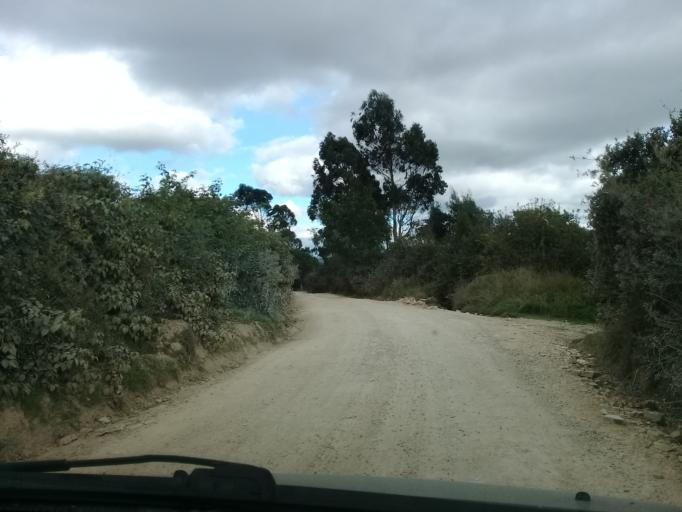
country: CO
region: Cundinamarca
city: Lenguazaque
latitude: 5.2877
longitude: -73.6817
